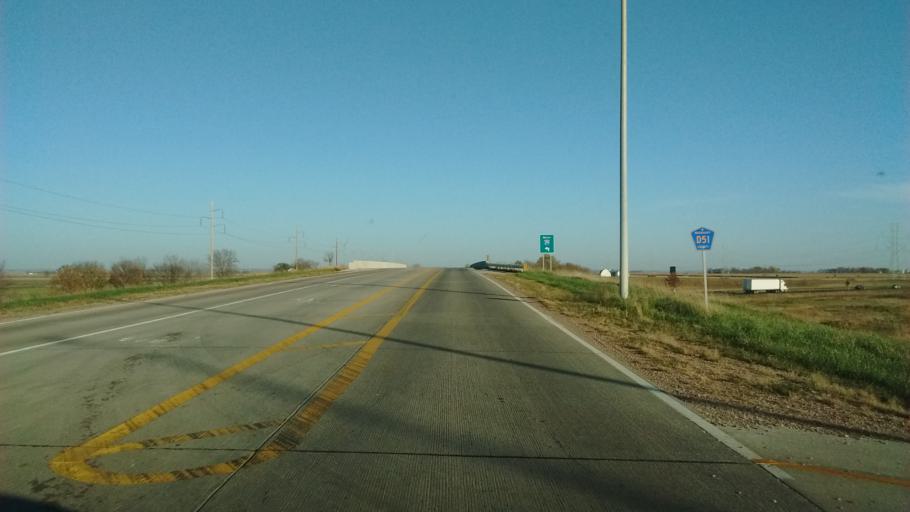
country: US
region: Iowa
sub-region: Woodbury County
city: Sergeant Bluff
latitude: 42.3299
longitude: -96.3206
